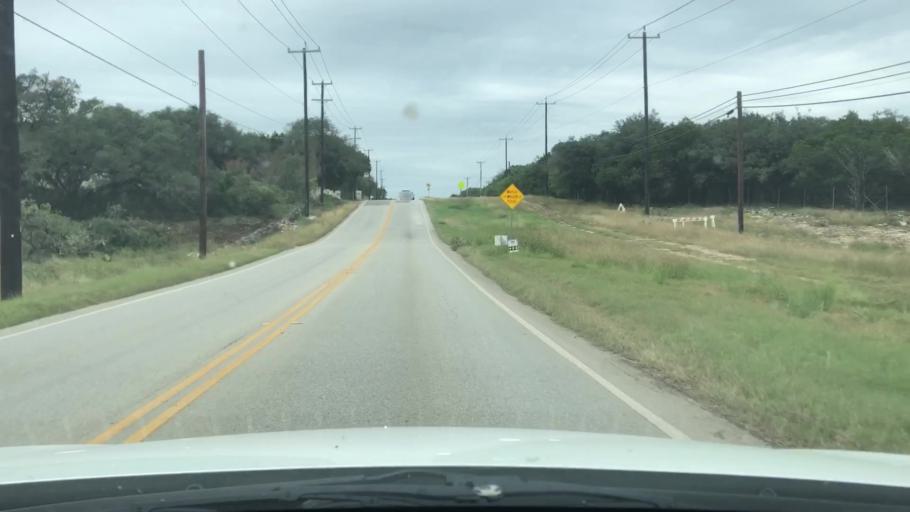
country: US
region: Texas
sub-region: Bexar County
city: Hollywood Park
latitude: 29.6466
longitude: -98.4066
